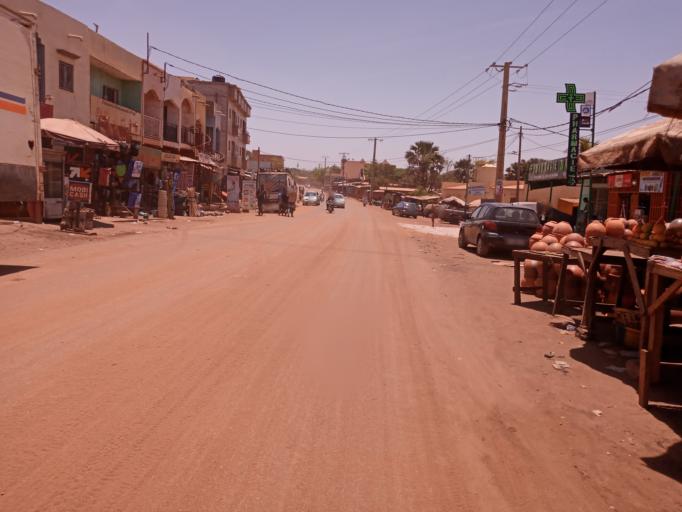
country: ML
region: Bamako
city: Bamako
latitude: 12.5808
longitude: -7.9720
